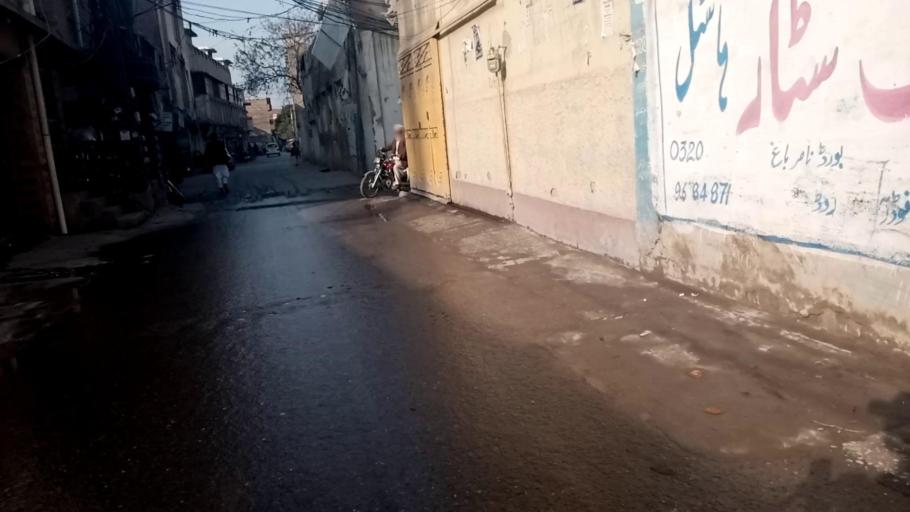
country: PK
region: Khyber Pakhtunkhwa
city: Peshawar
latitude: 34.0042
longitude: 71.4726
